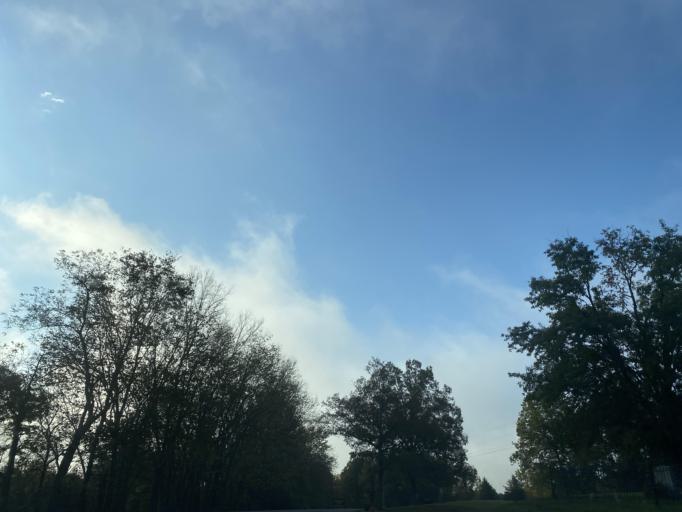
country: US
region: Kentucky
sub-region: Pendleton County
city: Falmouth
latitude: 38.7251
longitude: -84.2821
